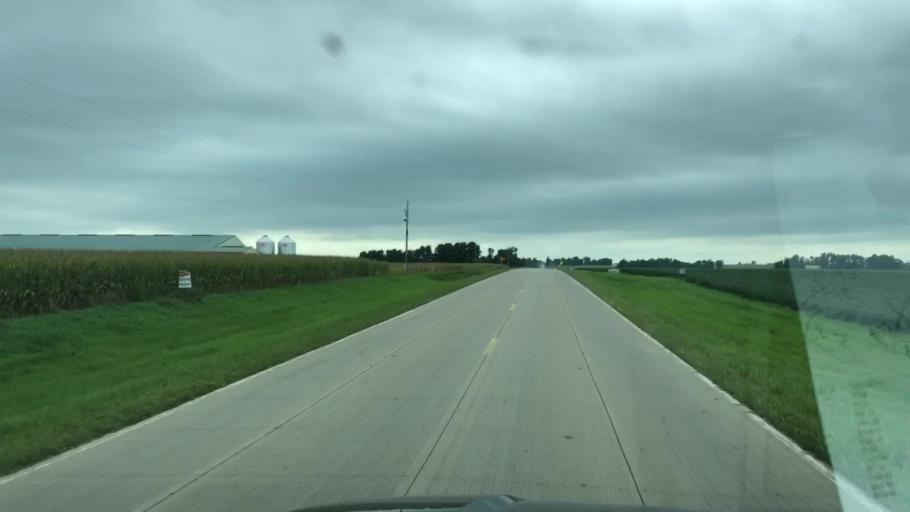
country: US
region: Iowa
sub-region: O'Brien County
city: Sheldon
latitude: 43.1251
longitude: -95.9790
